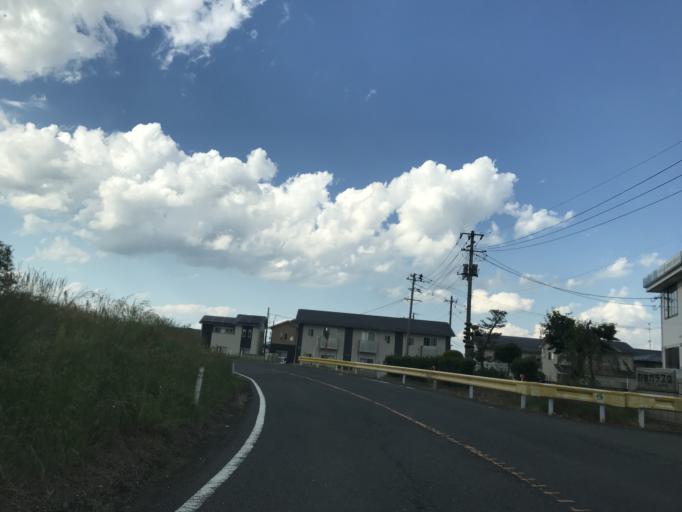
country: JP
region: Miyagi
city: Wakuya
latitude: 38.6785
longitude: 141.2087
